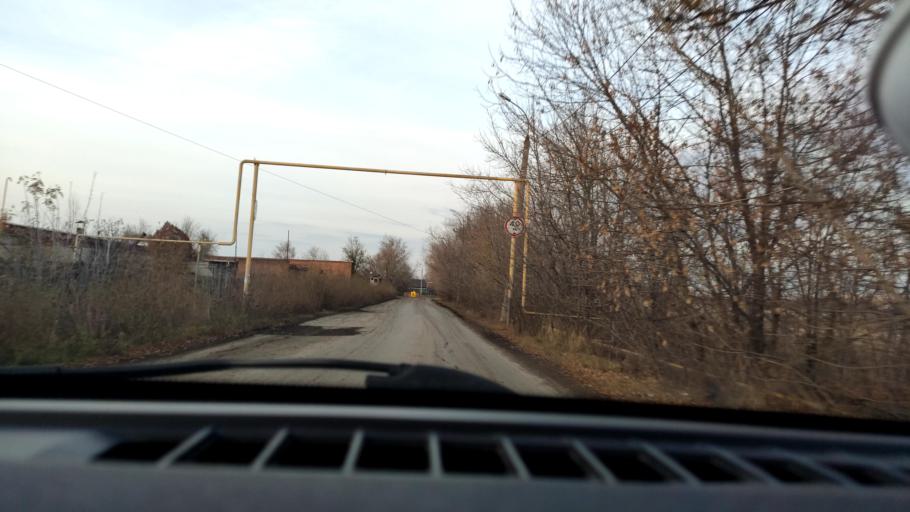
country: RU
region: Samara
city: Samara
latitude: 53.1355
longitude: 50.1365
